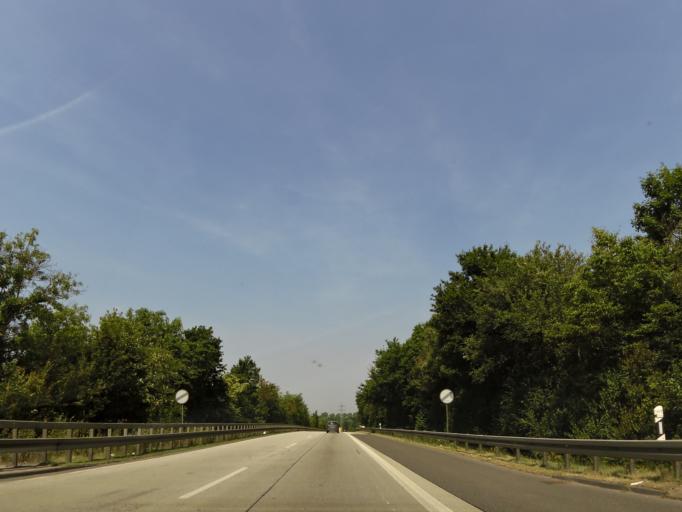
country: DE
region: North Rhine-Westphalia
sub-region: Regierungsbezirk Koln
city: Erftstadt
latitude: 50.8171
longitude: 6.7856
